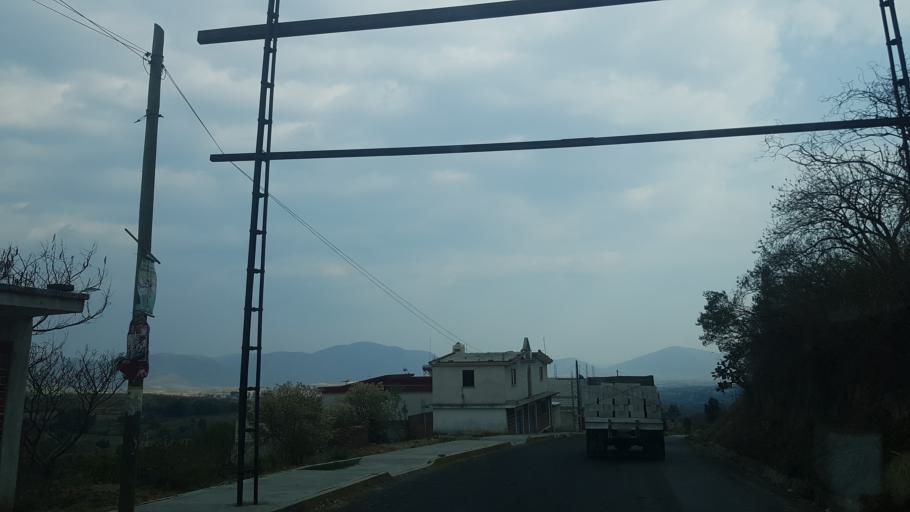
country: MX
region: Puebla
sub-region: Santa Isabel Cholula
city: San Martin Tlamapa
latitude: 18.9786
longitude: -98.3960
